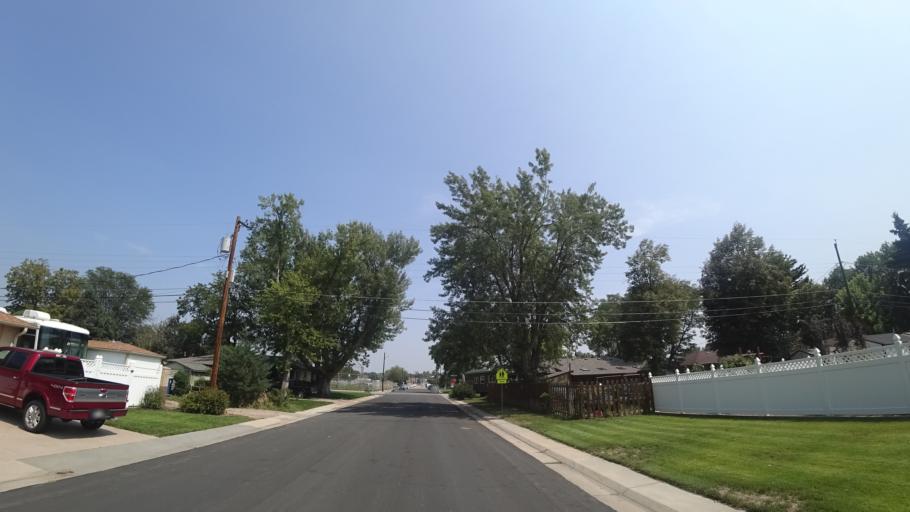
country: US
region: Colorado
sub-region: Arapahoe County
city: Englewood
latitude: 39.6259
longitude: -104.9935
